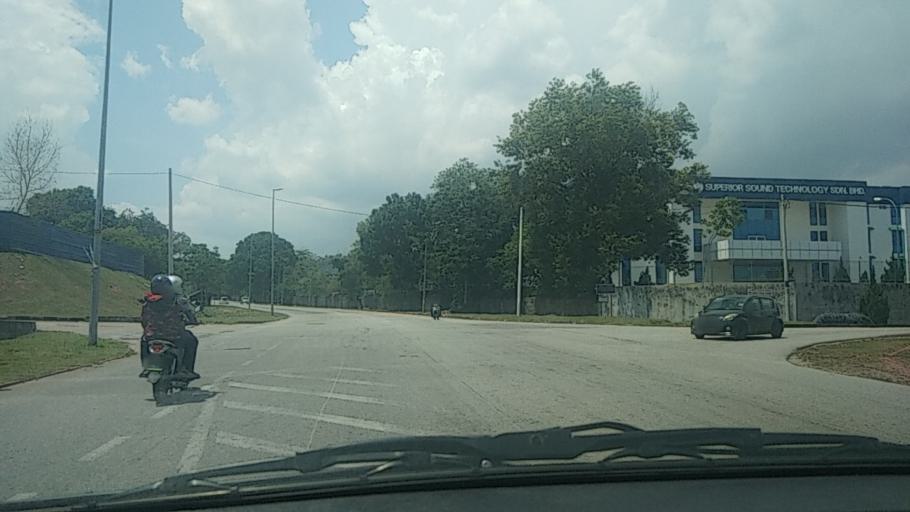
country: MY
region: Kedah
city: Sungai Petani
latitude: 5.6458
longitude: 100.5330
